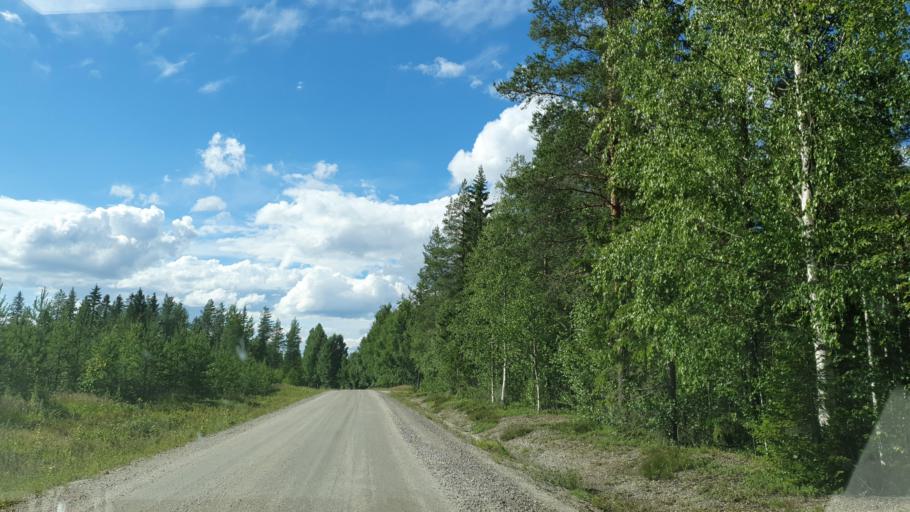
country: FI
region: Kainuu
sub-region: Kehys-Kainuu
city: Kuhmo
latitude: 64.1497
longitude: 29.7457
